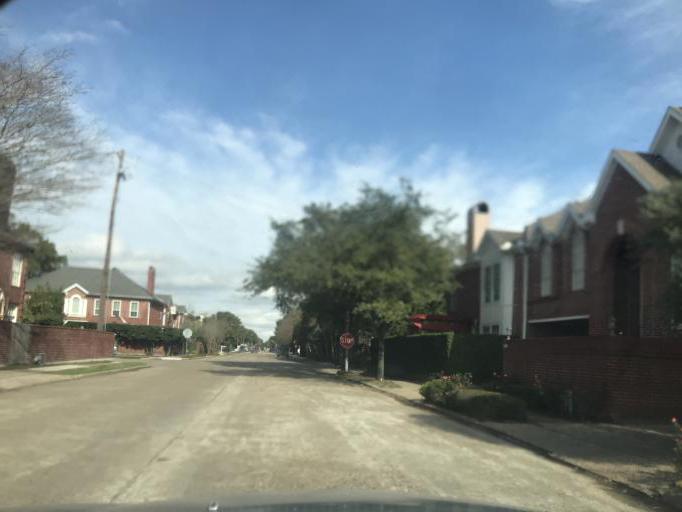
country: US
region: Texas
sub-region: Harris County
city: Hunters Creek Village
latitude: 29.7417
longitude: -95.4886
